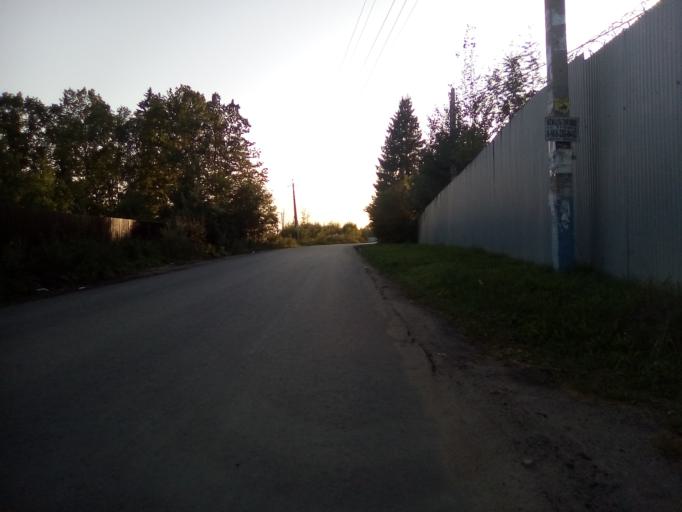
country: RU
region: Moskovskaya
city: Krasnoznamensk
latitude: 55.5743
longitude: 37.0287
